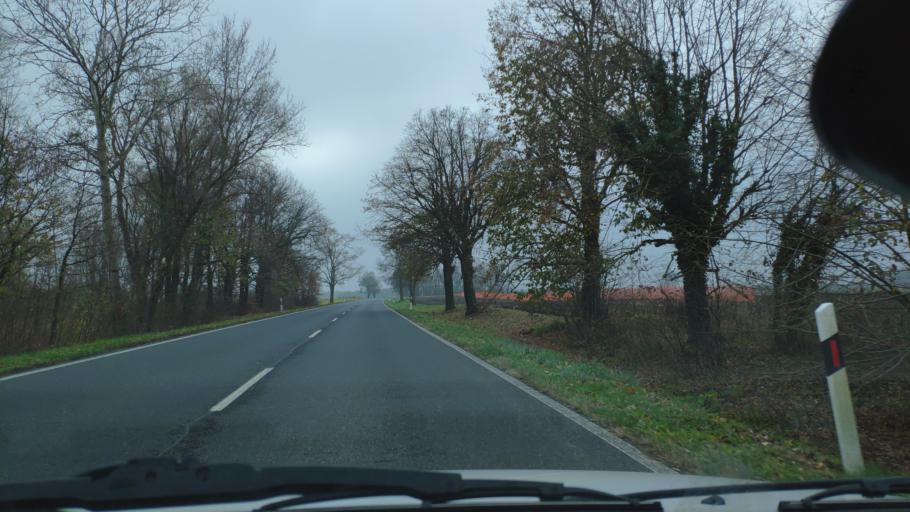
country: HU
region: Somogy
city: Balatonbereny
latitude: 46.6229
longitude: 17.2856
